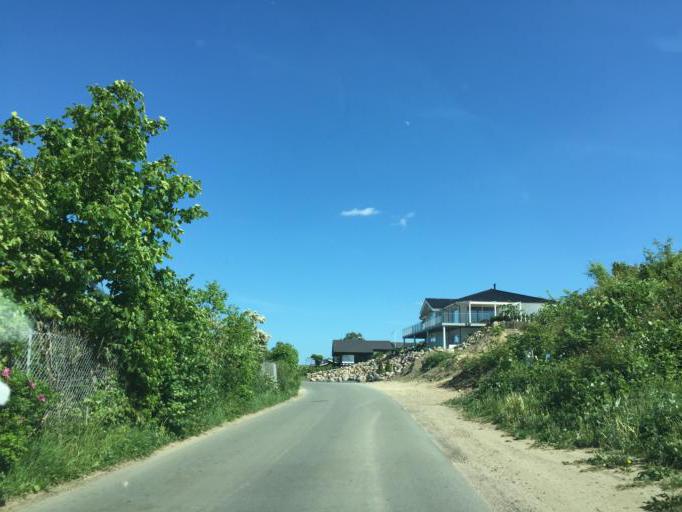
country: DK
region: Zealand
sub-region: Stevns Kommune
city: Stroby Egede
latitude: 55.4085
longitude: 12.2758
